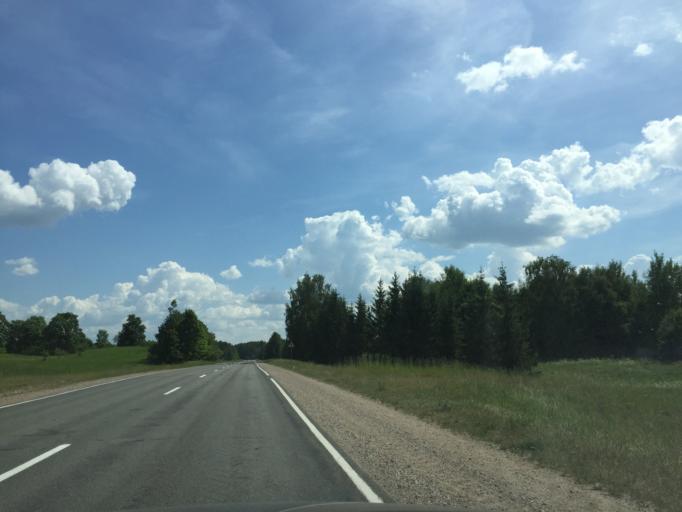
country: LV
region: Vilanu
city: Vilani
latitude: 56.5929
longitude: 26.8800
